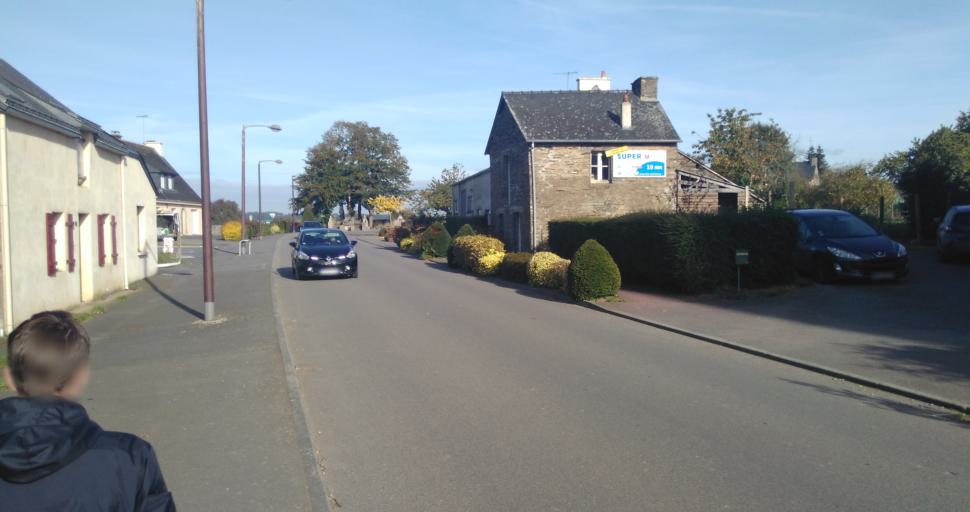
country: FR
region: Brittany
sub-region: Departement du Morbihan
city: Peillac
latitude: 47.7405
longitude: -2.2133
